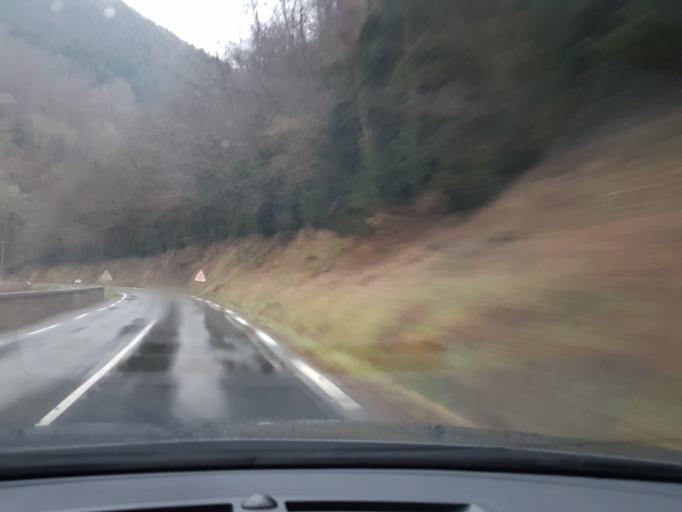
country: FR
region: Midi-Pyrenees
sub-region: Departement de l'Ariege
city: Saint-Girons
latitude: 42.9167
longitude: 1.1929
